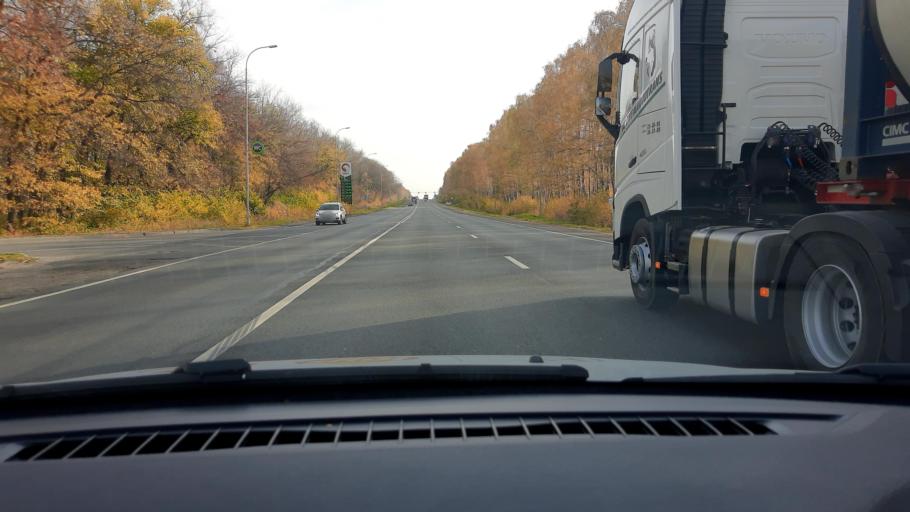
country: RU
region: Nizjnij Novgorod
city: Pamyat' Parizhskoy Kommuny
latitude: 56.0600
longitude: 44.3897
